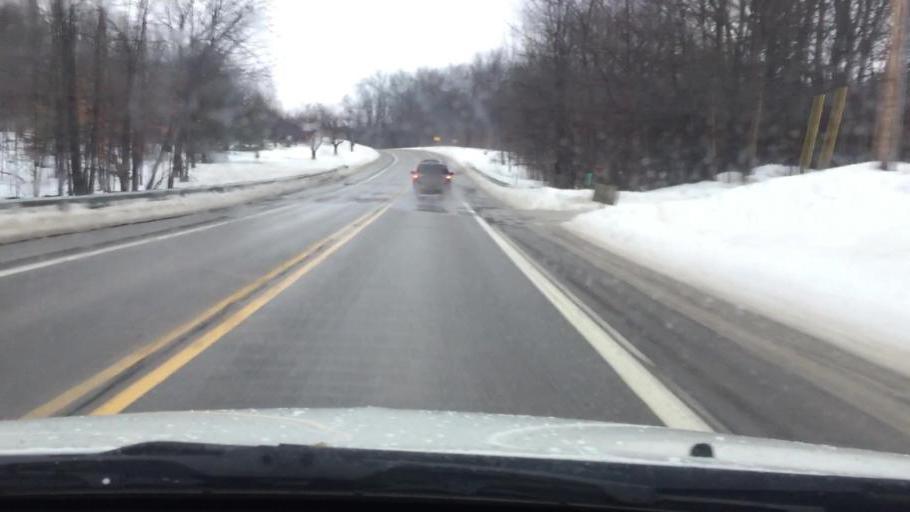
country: US
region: Michigan
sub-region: Charlevoix County
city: East Jordan
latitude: 45.2127
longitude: -85.1717
